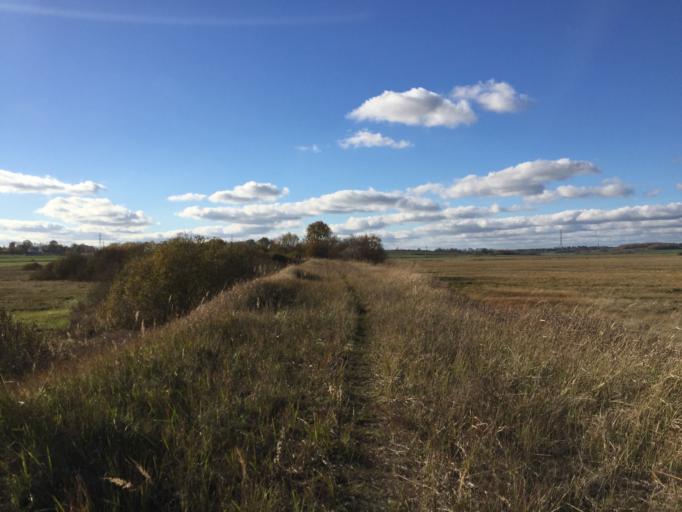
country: LV
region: Tukuma Rajons
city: Tukums
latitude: 56.9603
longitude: 23.0955
